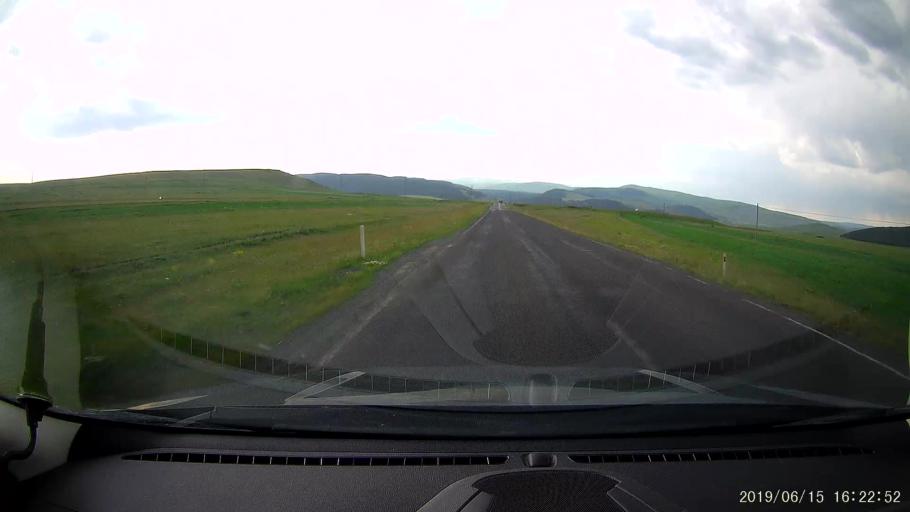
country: TR
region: Ardahan
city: Hanak
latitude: 41.1839
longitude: 42.8556
